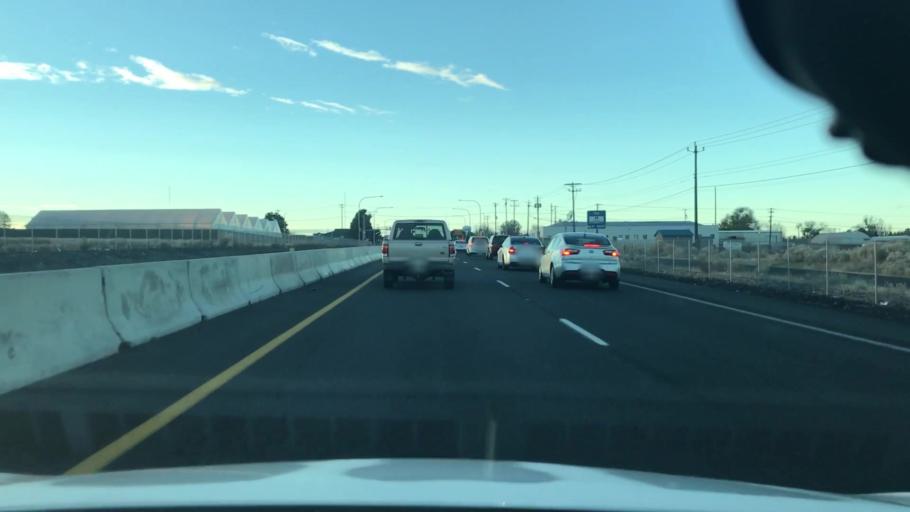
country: US
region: Washington
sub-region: Grant County
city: Moses Lake
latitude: 47.1341
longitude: -119.2569
